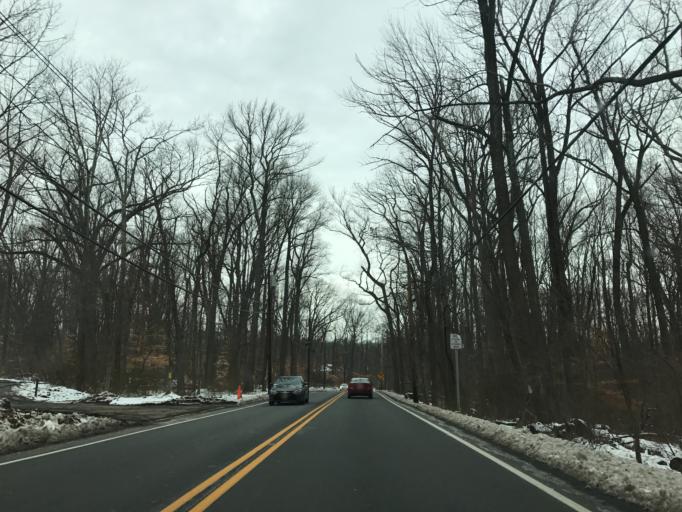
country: US
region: New Jersey
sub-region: Mercer County
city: Princeton
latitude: 40.3761
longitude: -74.6631
